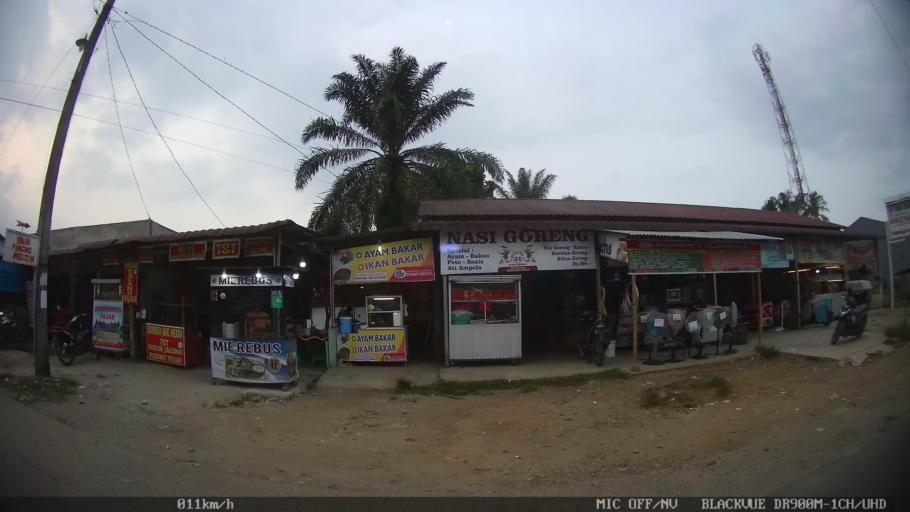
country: ID
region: North Sumatra
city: Sunggal
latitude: 3.5611
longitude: 98.5864
